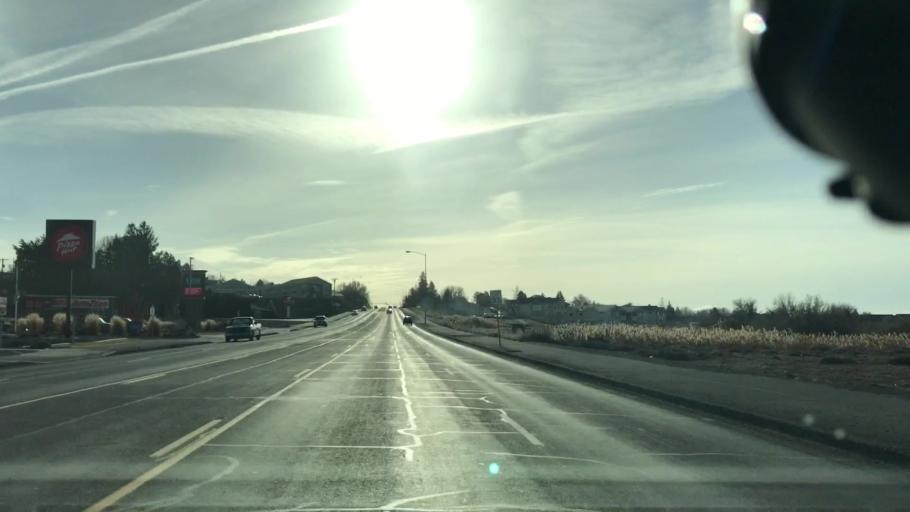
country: US
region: Washington
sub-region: Grant County
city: Moses Lake
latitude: 47.1282
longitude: -119.2694
